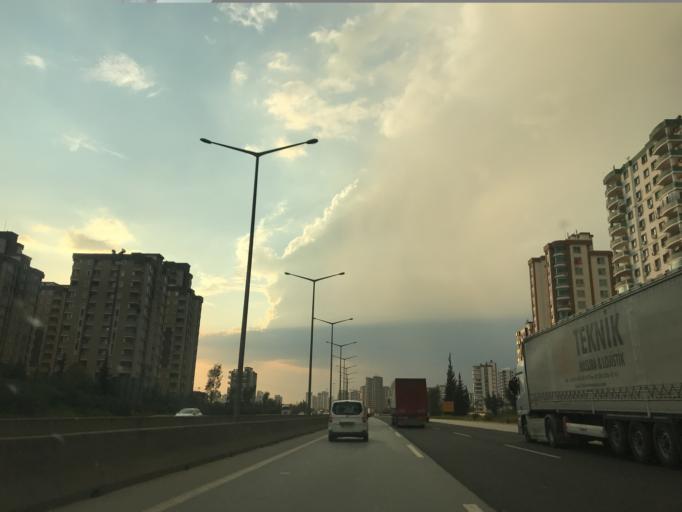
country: TR
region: Adana
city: Seyhan
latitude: 37.0320
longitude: 35.2598
